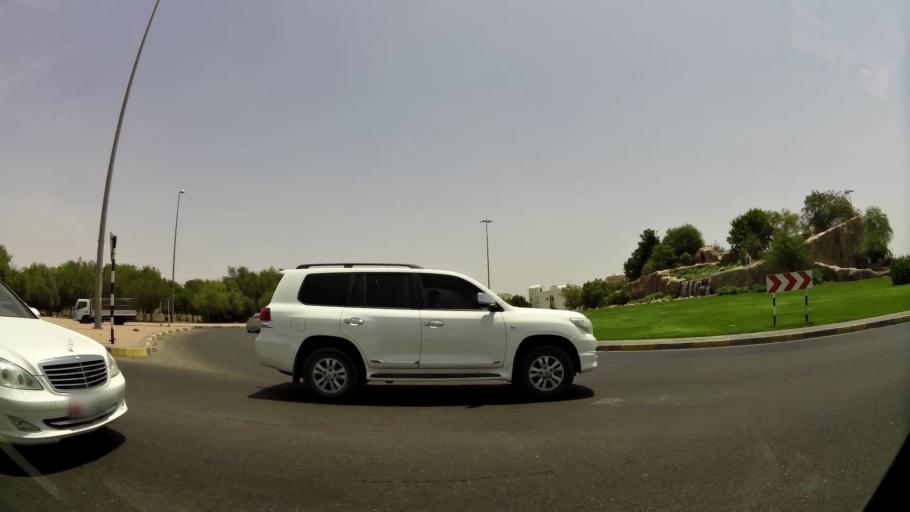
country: AE
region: Abu Dhabi
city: Al Ain
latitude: 24.2069
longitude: 55.7364
